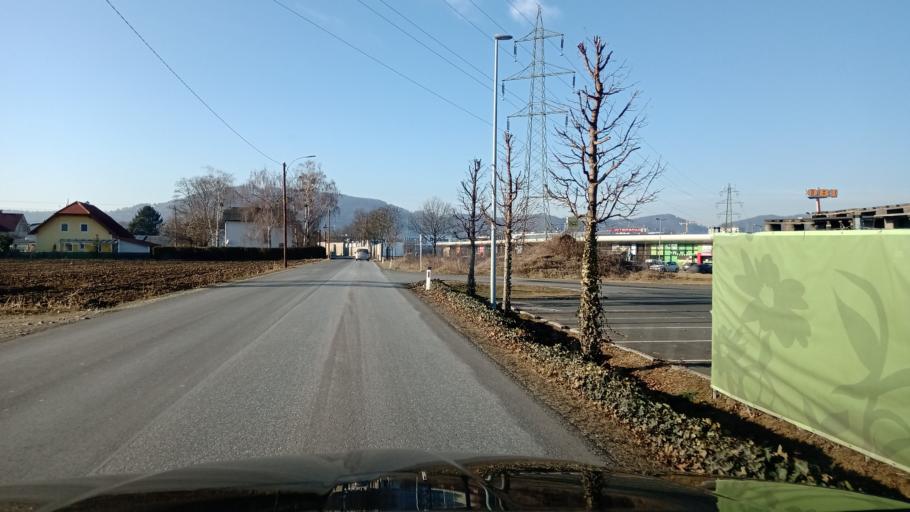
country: AT
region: Styria
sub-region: Politischer Bezirk Graz-Umgebung
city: Feldkirchen bei Graz
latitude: 47.0309
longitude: 15.4221
